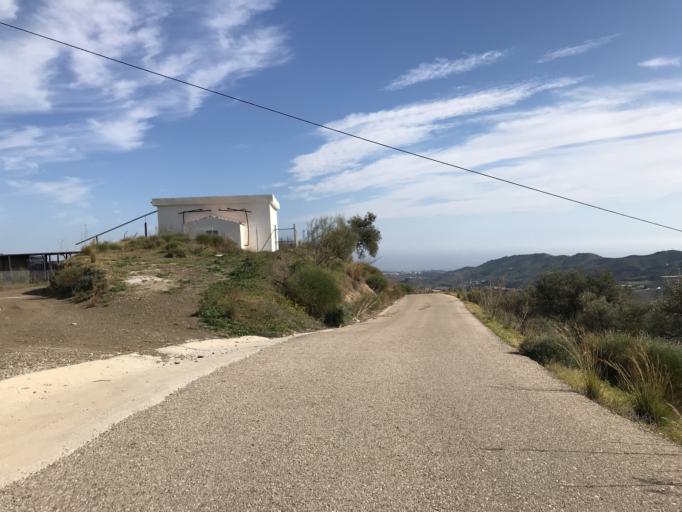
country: ES
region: Andalusia
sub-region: Provincia de Malaga
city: Valdes
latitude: 36.7740
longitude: -4.2161
